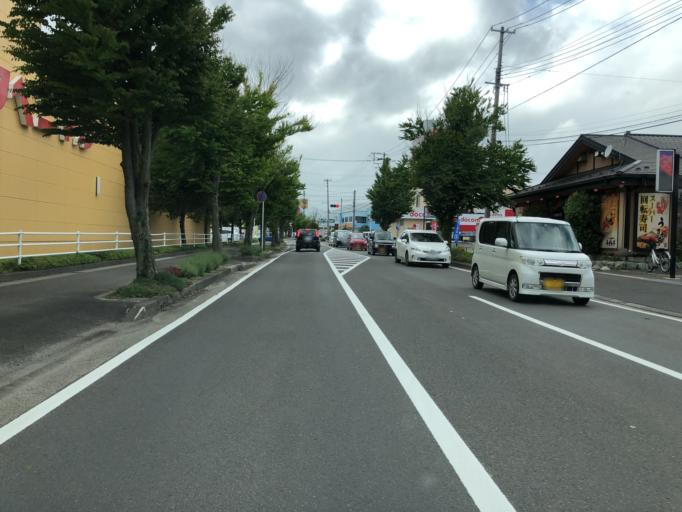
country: JP
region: Fukushima
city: Fukushima-shi
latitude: 37.7702
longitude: 140.4372
